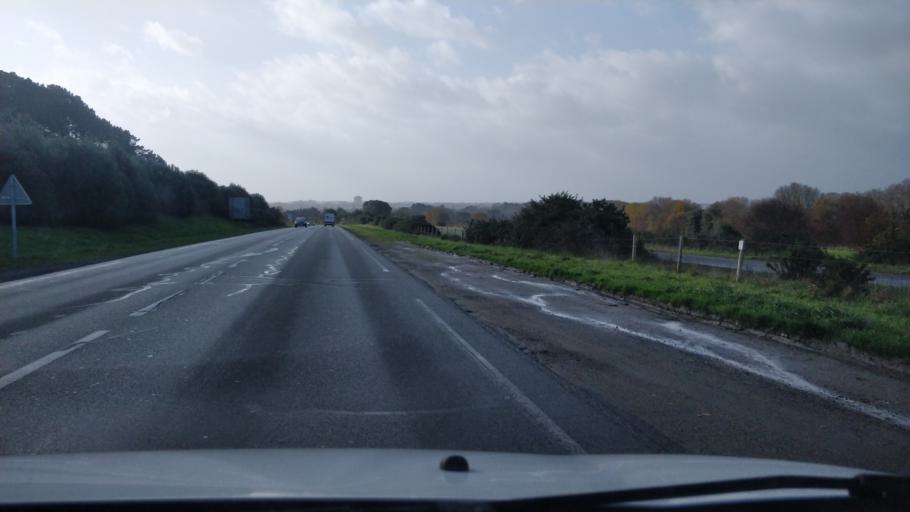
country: FR
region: Pays de la Loire
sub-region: Departement de la Loire-Atlantique
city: La Baule-Escoublac
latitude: 47.3063
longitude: -2.3908
